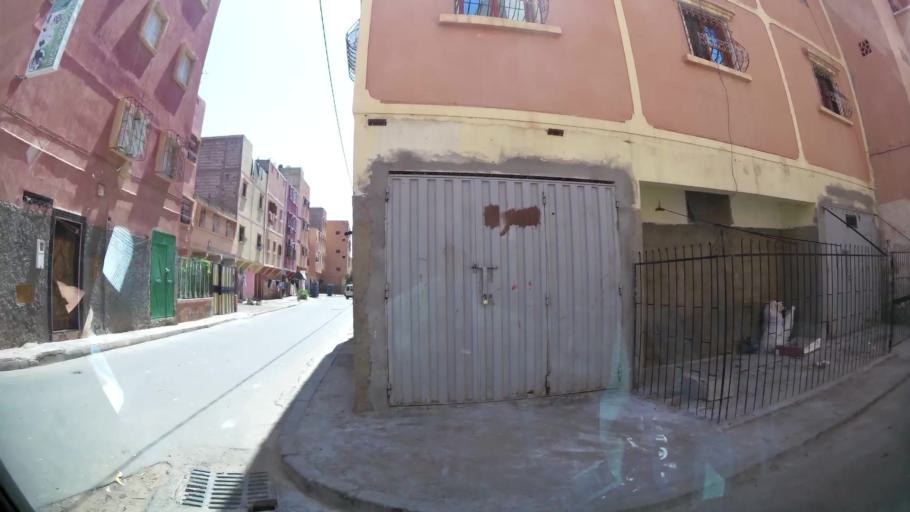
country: MA
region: Souss-Massa-Draa
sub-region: Inezgane-Ait Mellou
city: Inezgane
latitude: 30.3430
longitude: -9.4872
